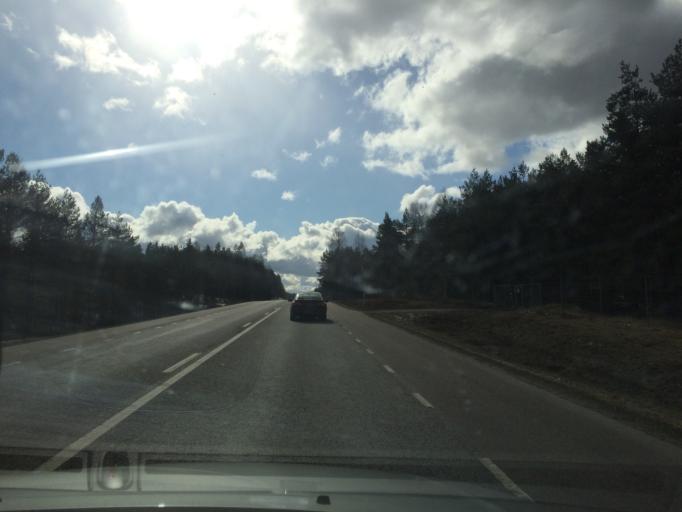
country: SE
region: Vaestra Goetaland
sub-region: Gotene Kommun
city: Goetene
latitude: 58.6027
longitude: 13.6407
